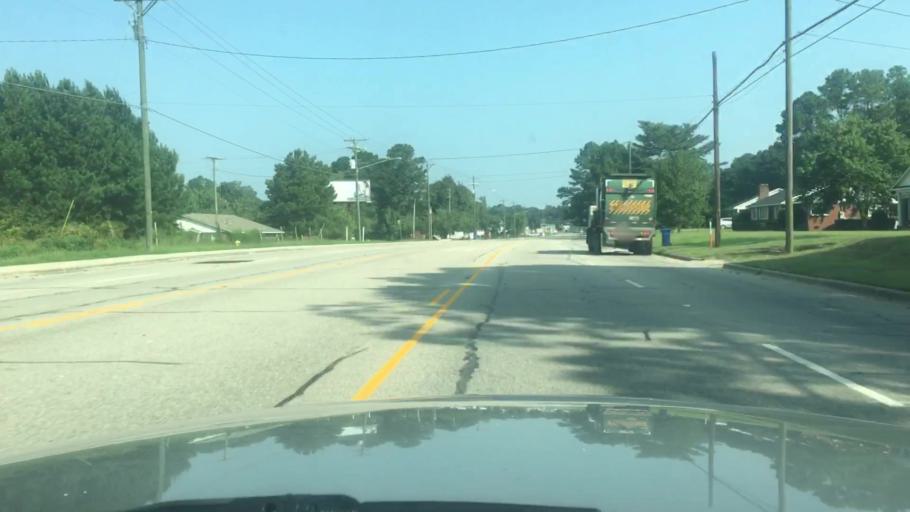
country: US
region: North Carolina
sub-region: Cumberland County
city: Fayetteville
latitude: 35.0234
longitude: -78.8415
